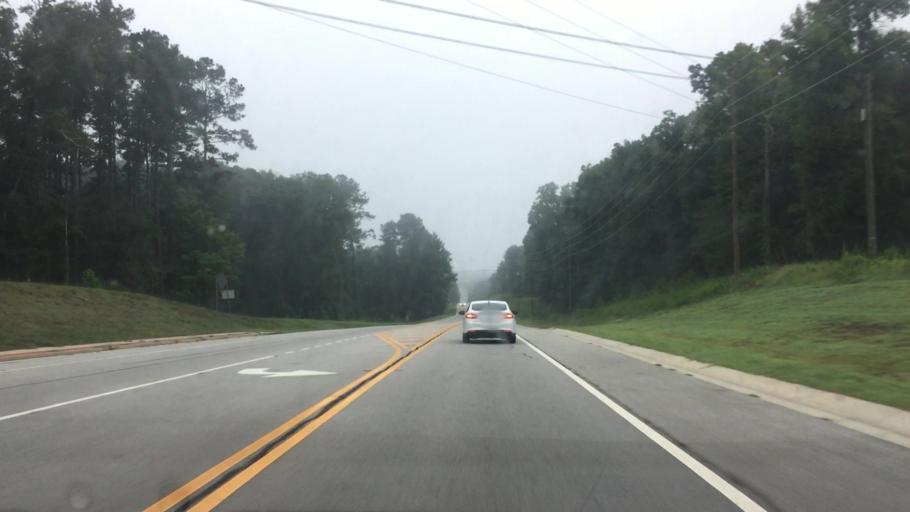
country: US
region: Georgia
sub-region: Henry County
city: Stockbridge
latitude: 33.5500
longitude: -84.1377
